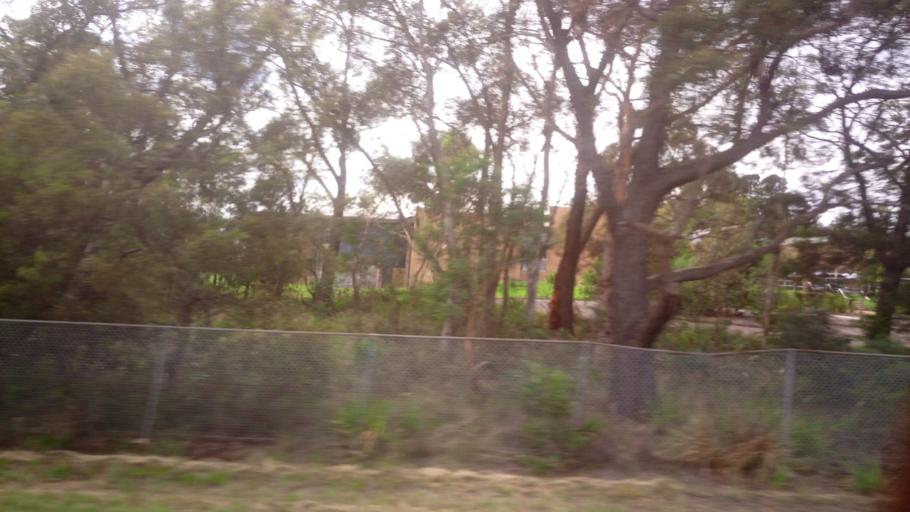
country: AU
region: New South Wales
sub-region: Blue Mountains Municipality
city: Leura
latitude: -33.7074
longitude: 150.3670
